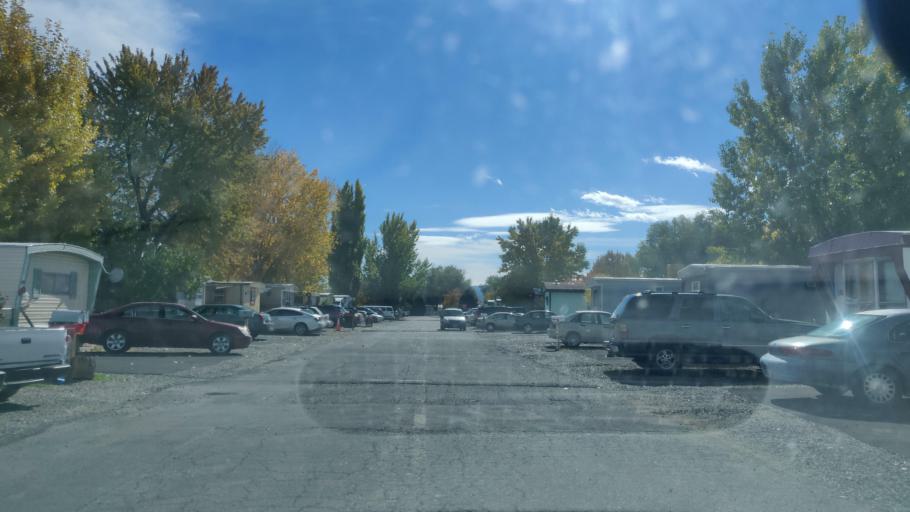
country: US
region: Colorado
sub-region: Mesa County
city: Fruitvale
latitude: 39.0804
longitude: -108.5125
